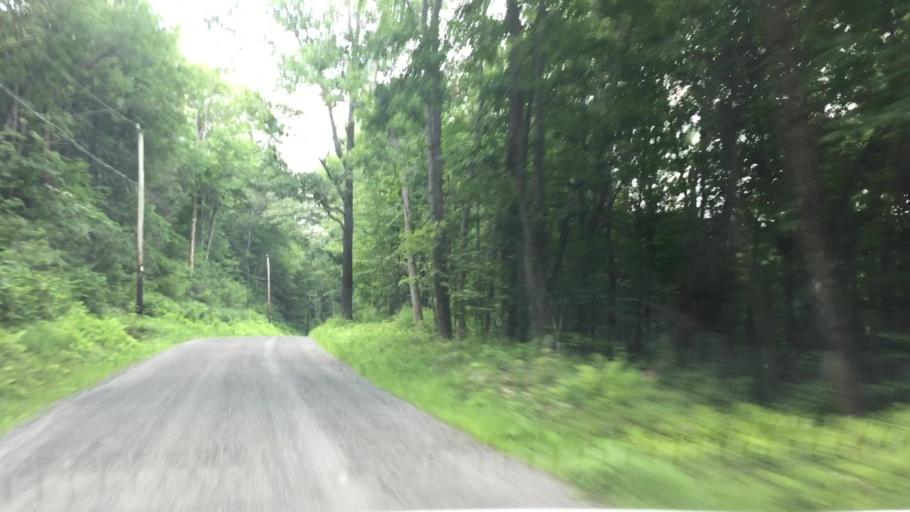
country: US
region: Massachusetts
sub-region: Berkshire County
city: Lee
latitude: 42.2733
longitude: -73.1889
